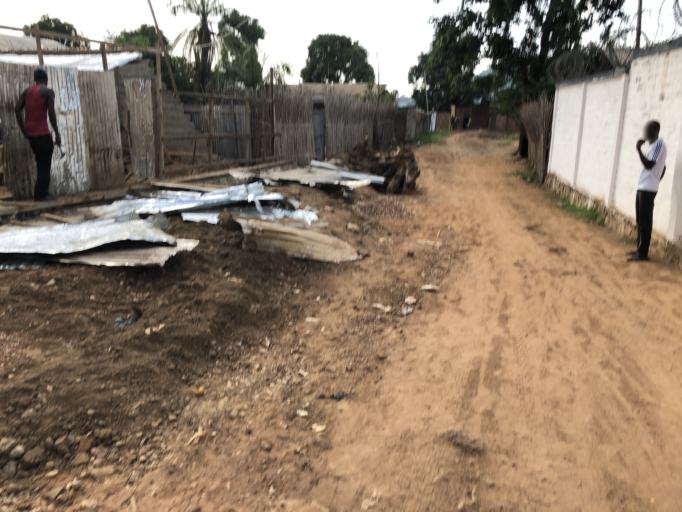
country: CF
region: Bangui
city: Bangui
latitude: 4.3516
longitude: 18.5970
